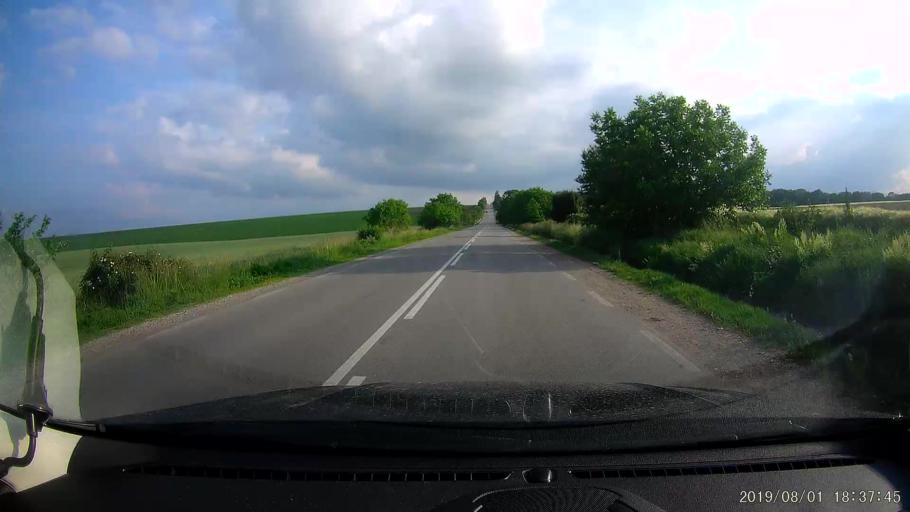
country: BG
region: Shumen
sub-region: Obshtina Khitrino
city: Gara Khitrino
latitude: 43.4146
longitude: 26.9259
